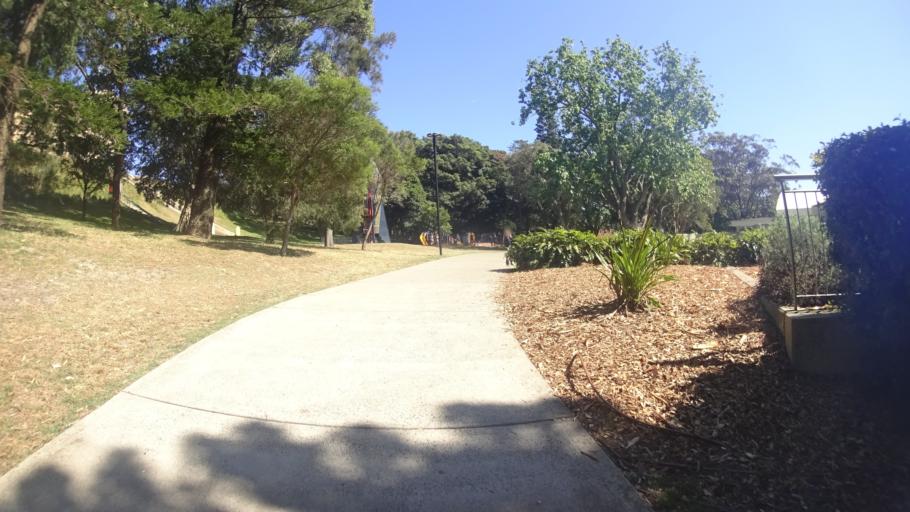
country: AU
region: New South Wales
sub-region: Waverley
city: Bondi
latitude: -33.8947
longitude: 151.2578
